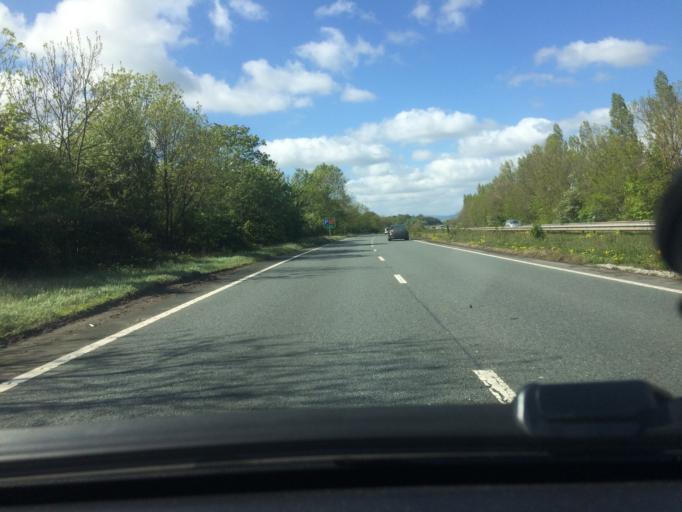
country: GB
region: England
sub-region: Cheshire West and Chester
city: Eccleston
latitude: 53.1668
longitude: -2.8684
